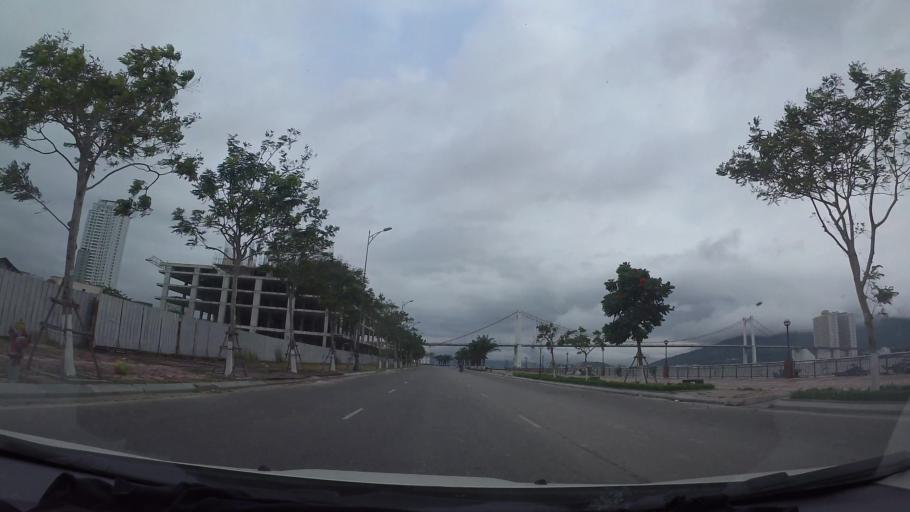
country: VN
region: Da Nang
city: Da Nang
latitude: 16.0893
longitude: 108.2202
